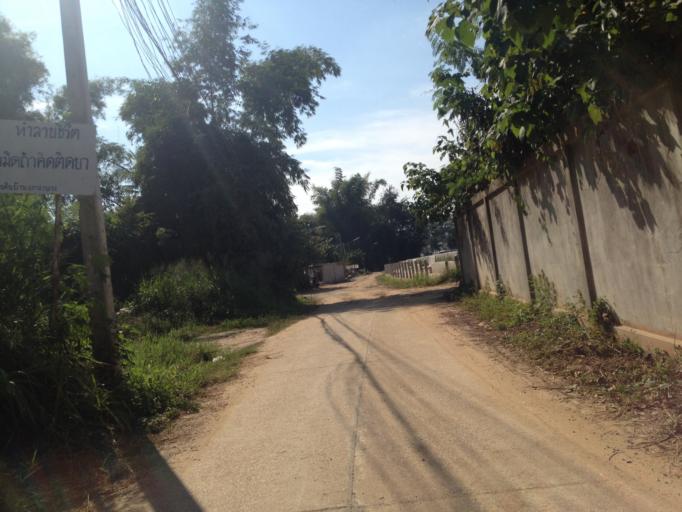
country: TH
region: Chiang Mai
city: Chiang Mai
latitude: 18.7405
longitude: 98.9836
